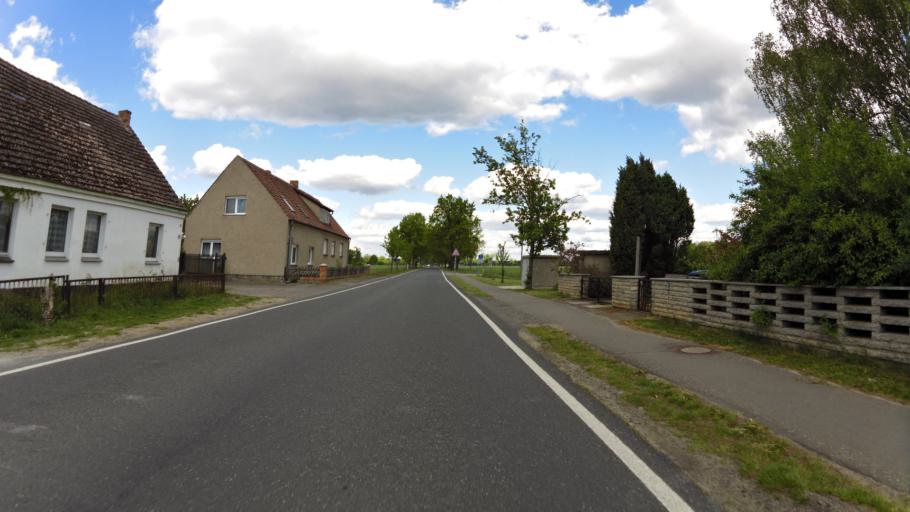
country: DE
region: Brandenburg
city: Schlepzig
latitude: 52.0845
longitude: 13.8934
